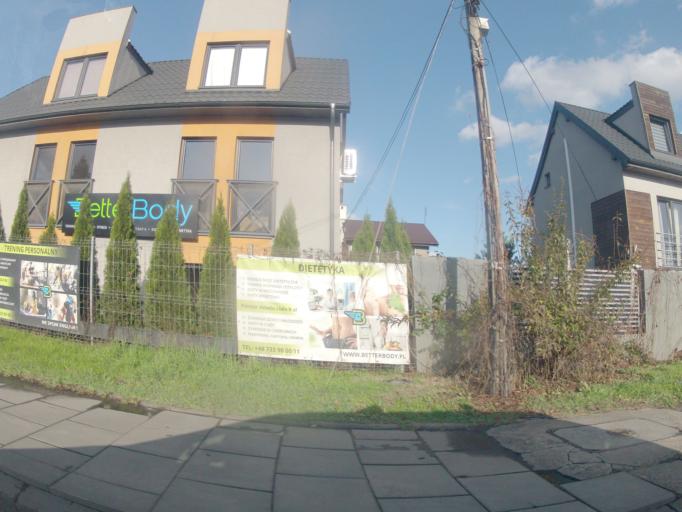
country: PL
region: Lesser Poland Voivodeship
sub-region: Powiat krakowski
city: Rzaska
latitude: 50.0641
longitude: 19.8829
